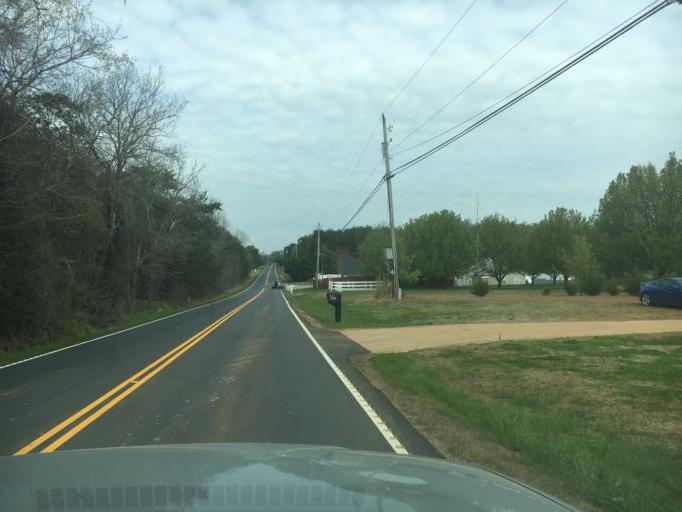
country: US
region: South Carolina
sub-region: Spartanburg County
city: Inman
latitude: 35.0153
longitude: -82.0779
